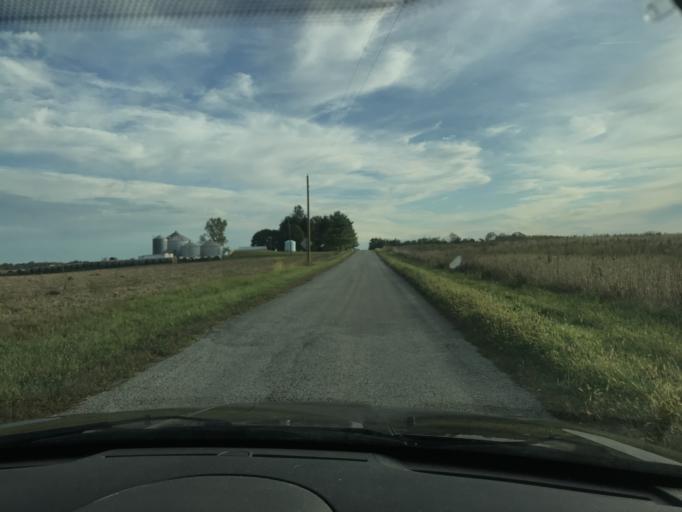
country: US
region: Ohio
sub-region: Logan County
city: West Liberty
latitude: 40.2100
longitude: -83.8085
